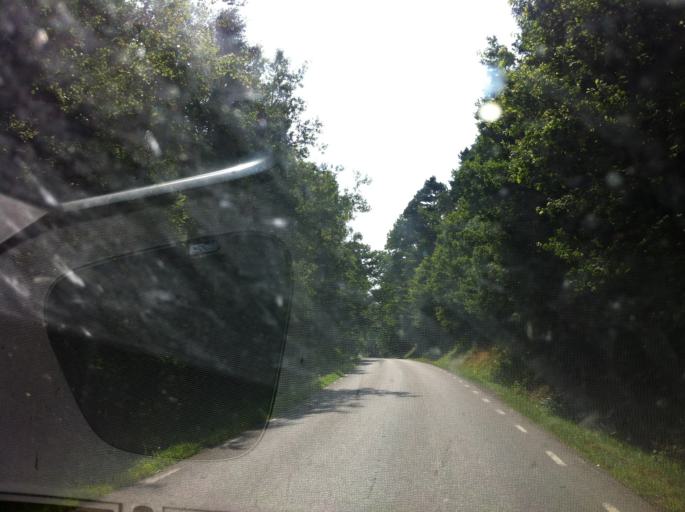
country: SE
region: Skane
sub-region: Hoors Kommun
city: Hoeoer
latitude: 55.9969
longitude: 13.4735
